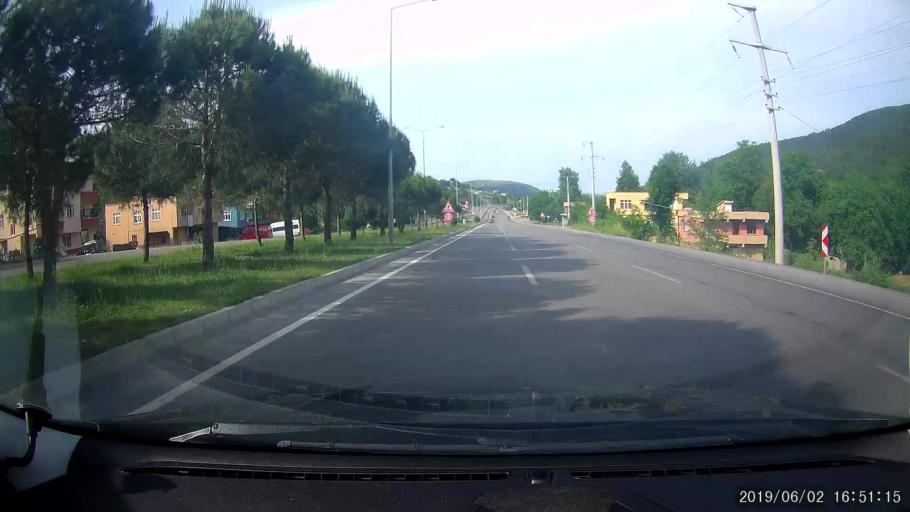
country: TR
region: Samsun
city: Taflan
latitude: 41.2712
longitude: 36.1799
